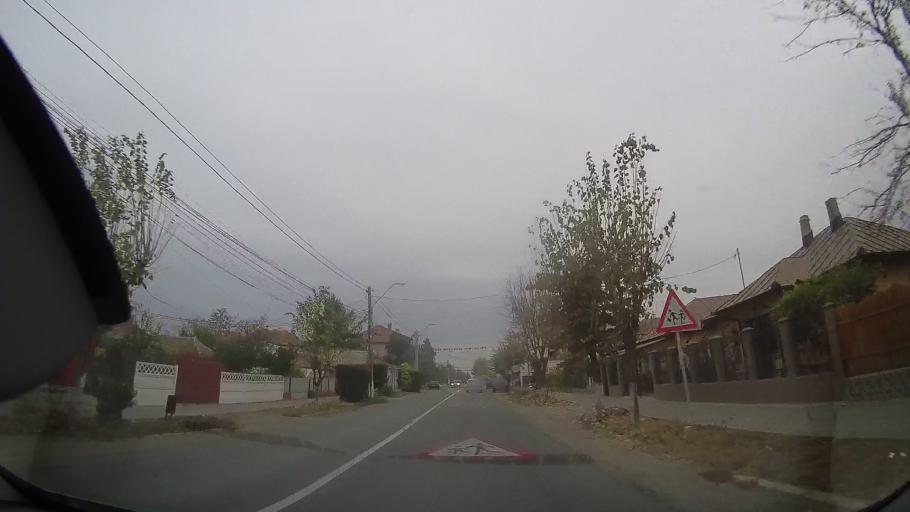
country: RO
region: Ialomita
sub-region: Oras Amara
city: Amara
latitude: 44.6200
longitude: 27.3141
